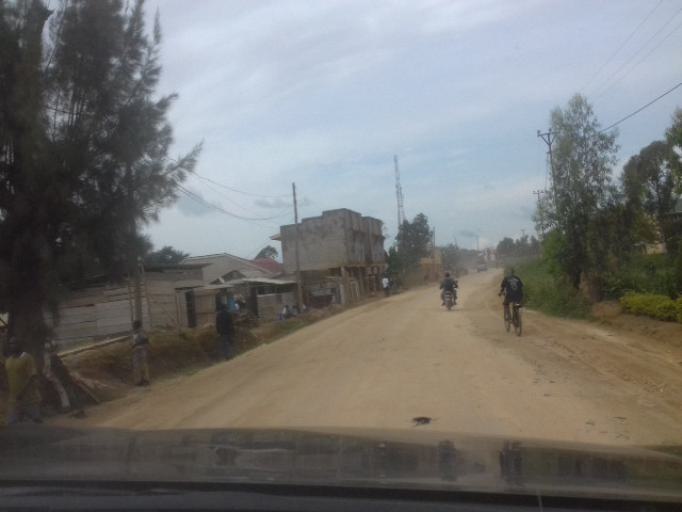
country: CD
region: Eastern Province
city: Bunia
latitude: 1.5378
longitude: 30.2527
